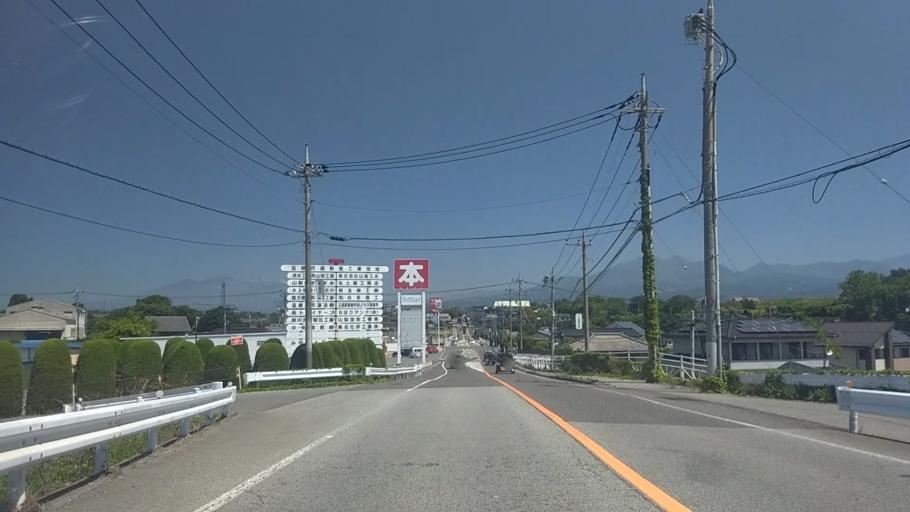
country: JP
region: Yamanashi
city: Nirasaki
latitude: 35.6726
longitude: 138.4648
